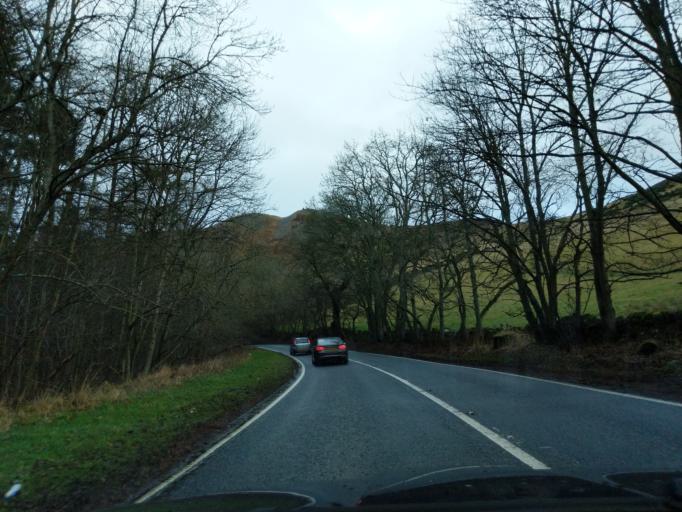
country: GB
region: Scotland
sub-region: The Scottish Borders
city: Galashiels
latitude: 55.6607
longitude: -2.8605
